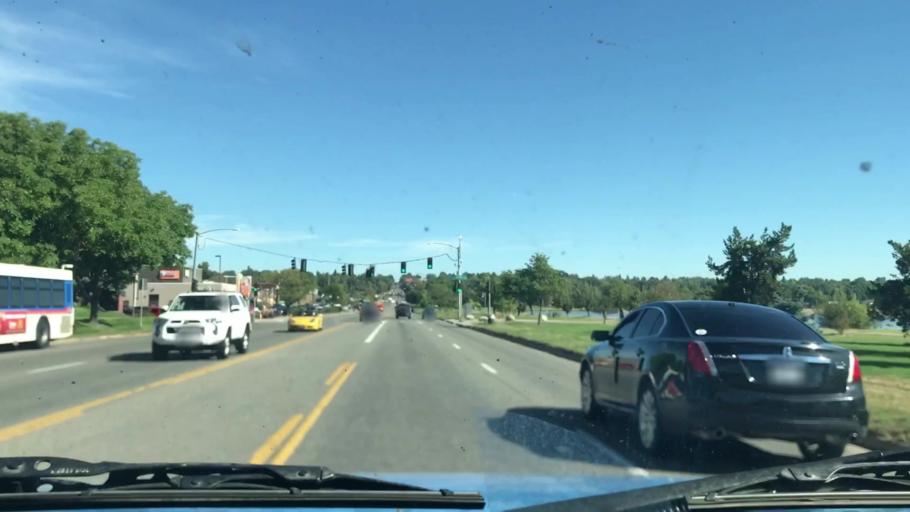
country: US
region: Colorado
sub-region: Jefferson County
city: Edgewater
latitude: 39.7466
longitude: -105.0532
